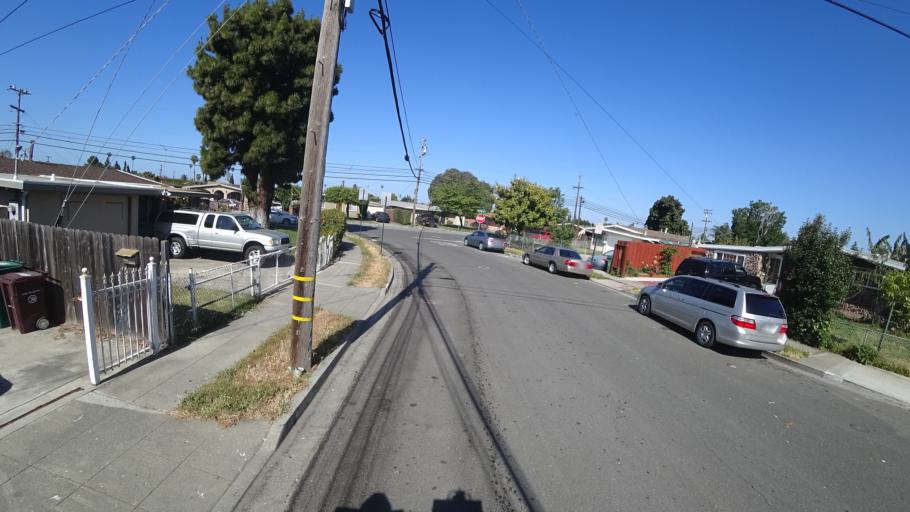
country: US
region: California
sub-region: Alameda County
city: Hayward
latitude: 37.6274
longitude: -122.0800
